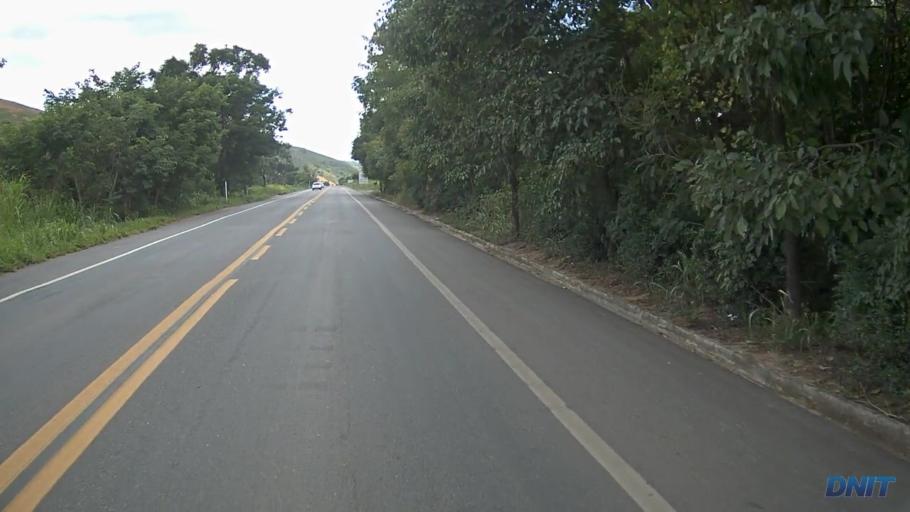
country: BR
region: Minas Gerais
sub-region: Governador Valadares
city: Governador Valadares
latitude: -18.9369
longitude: -42.0533
